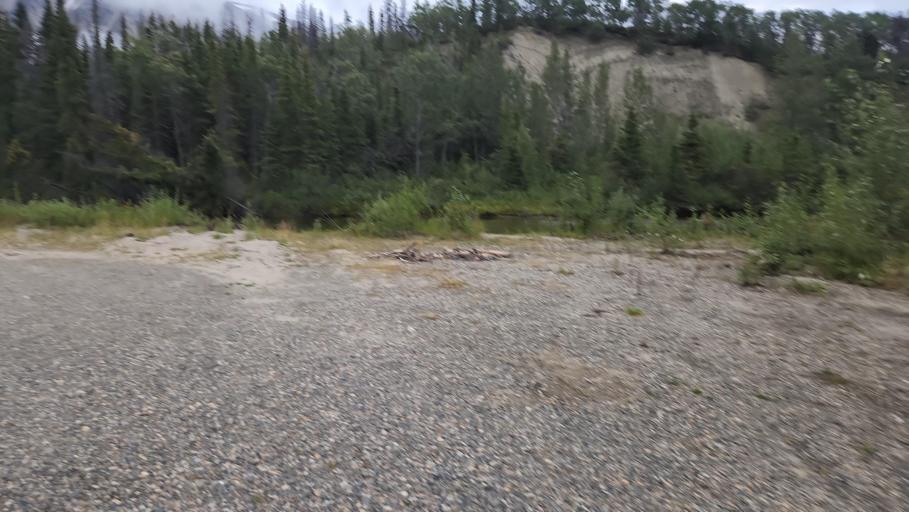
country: CA
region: Yukon
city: Haines Junction
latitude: 60.1107
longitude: -136.9309
